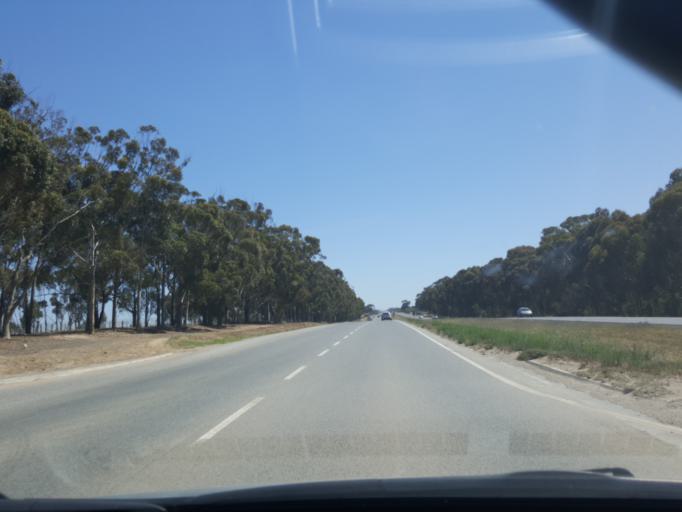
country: ZA
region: Western Cape
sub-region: City of Cape Town
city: Sunset Beach
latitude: -33.7750
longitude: 18.5483
